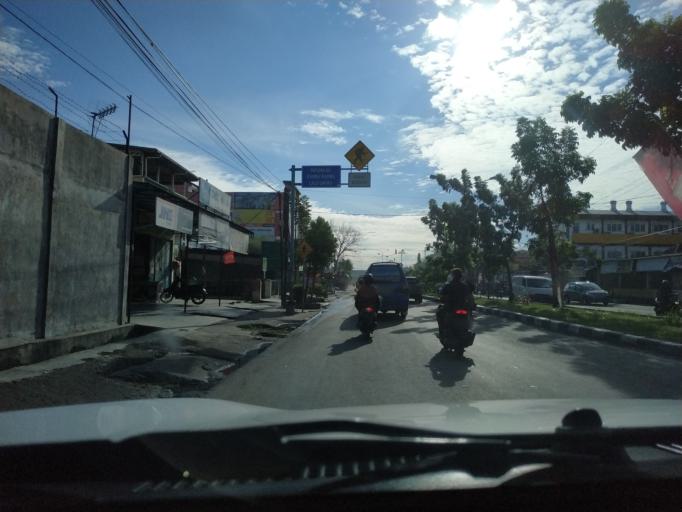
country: ID
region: North Sumatra
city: Medan
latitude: 3.5975
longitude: 98.7213
